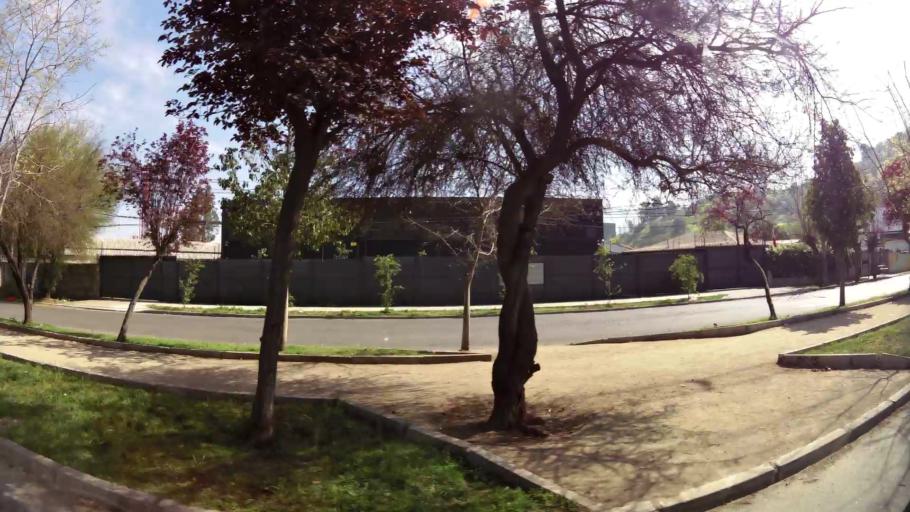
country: CL
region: Santiago Metropolitan
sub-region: Provincia de Santiago
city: Santiago
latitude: -33.4004
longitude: -70.6214
